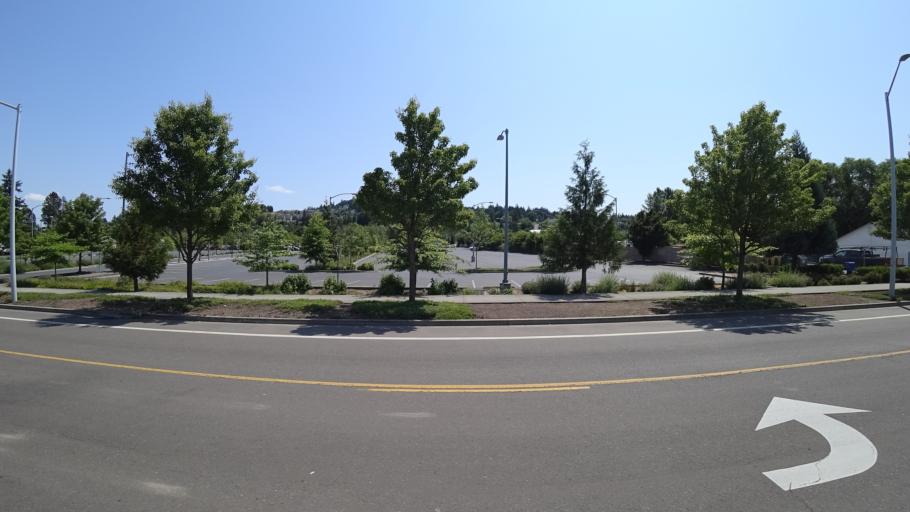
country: US
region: Oregon
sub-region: Multnomah County
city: Lents
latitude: 45.4531
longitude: -122.5762
